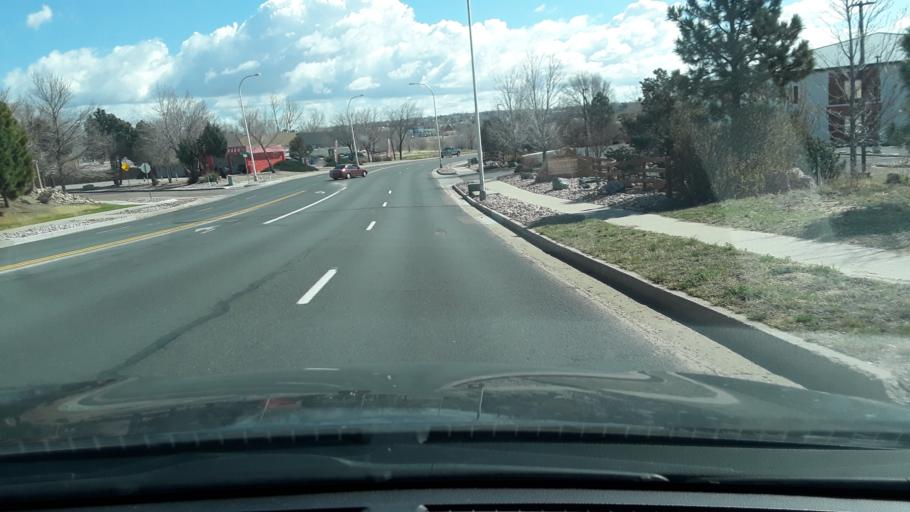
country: US
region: Colorado
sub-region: El Paso County
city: Cimarron Hills
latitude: 38.8564
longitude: -104.7264
